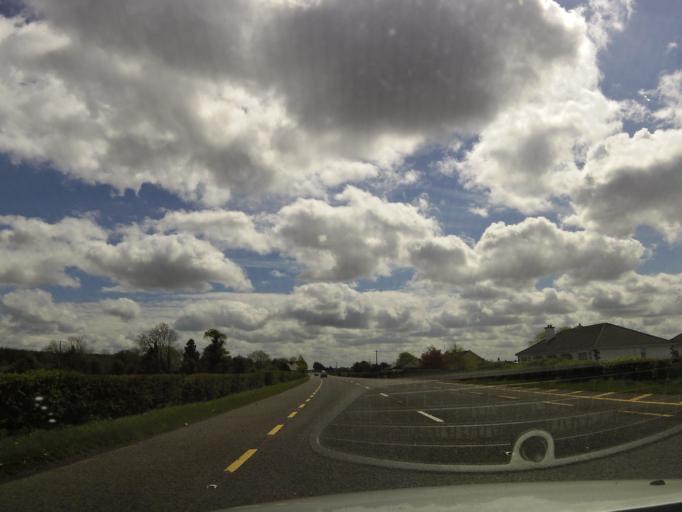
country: IE
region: Connaught
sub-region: Maigh Eo
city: Claremorris
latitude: 53.6819
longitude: -8.9689
